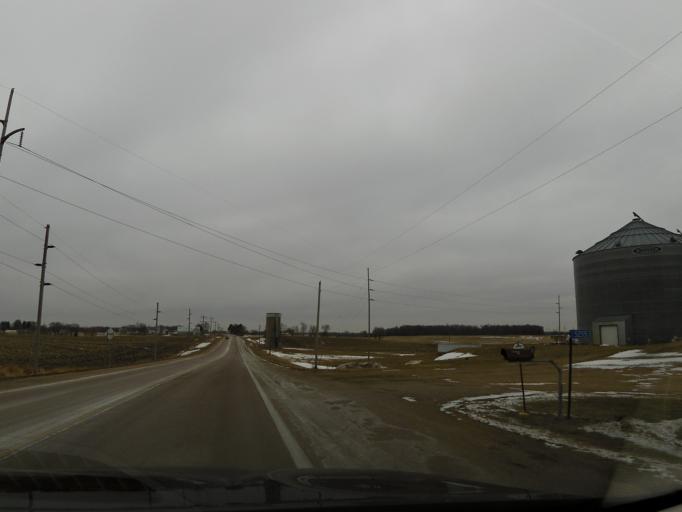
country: US
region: Minnesota
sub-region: Carver County
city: Watertown
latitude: 44.9073
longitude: -93.8193
